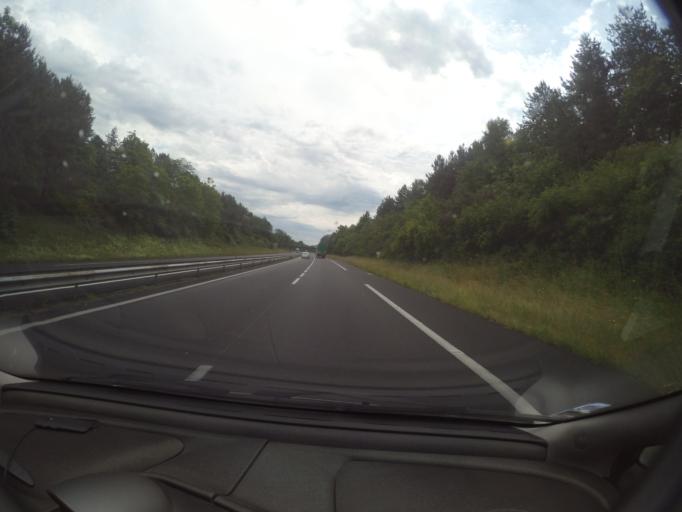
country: FR
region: Pays de la Loire
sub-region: Departement de Maine-et-Loire
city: Seiches-sur-le-Loir
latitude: 47.5715
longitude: -0.3341
